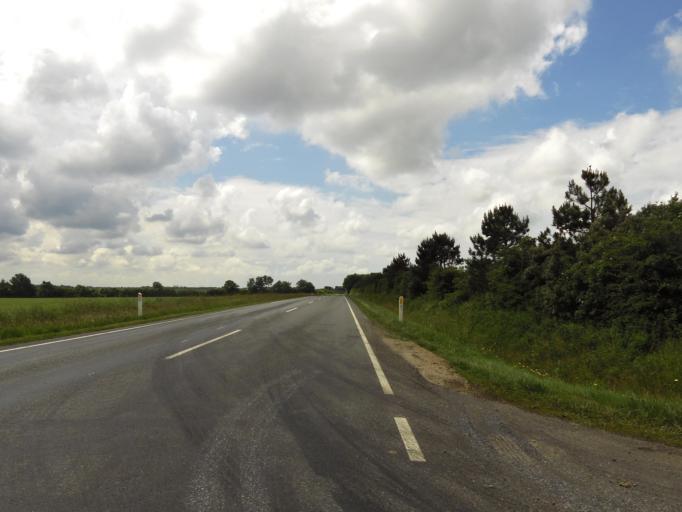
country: DK
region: South Denmark
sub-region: Haderslev Kommune
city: Gram
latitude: 55.2268
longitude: 8.9217
